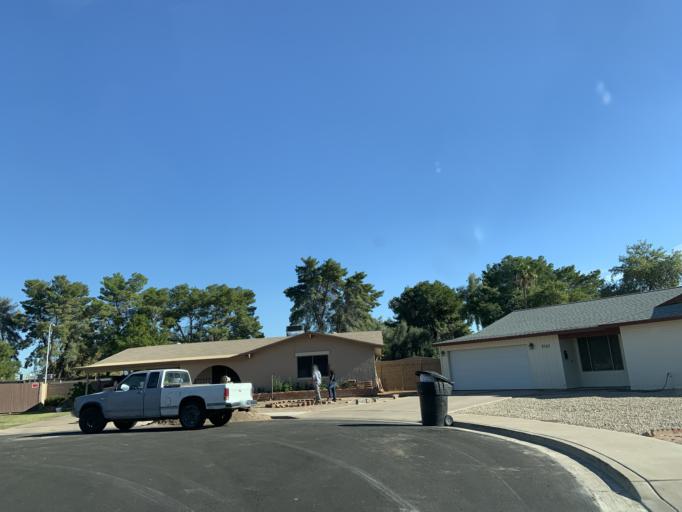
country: US
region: Arizona
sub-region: Maricopa County
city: Tempe
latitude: 33.4018
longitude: -111.8770
